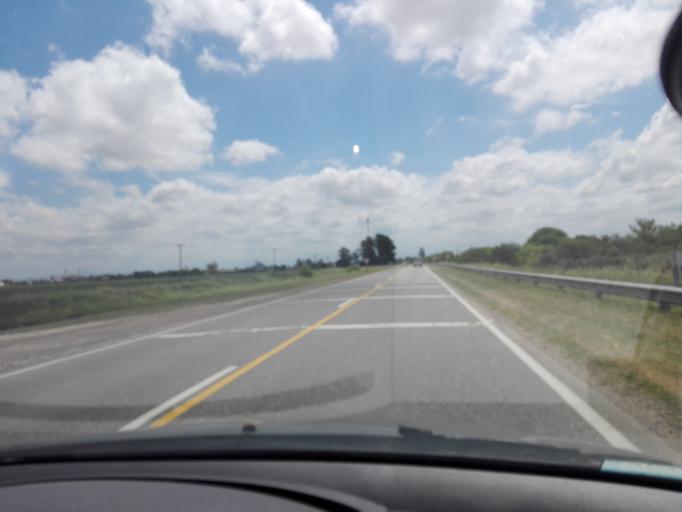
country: AR
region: Cordoba
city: Toledo
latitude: -31.6473
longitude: -64.0776
